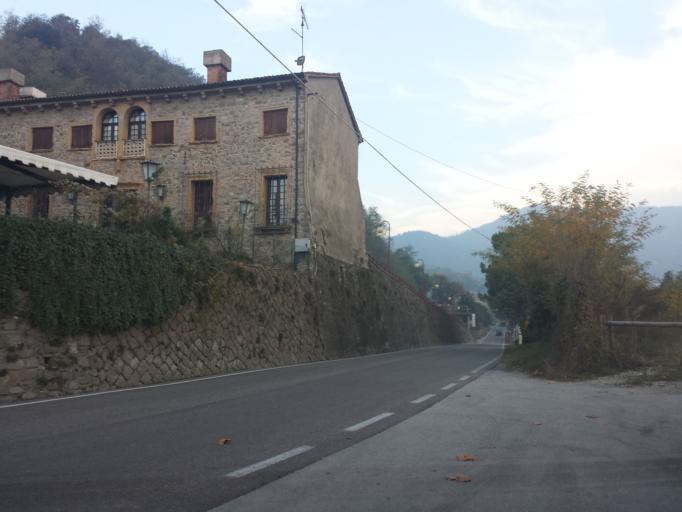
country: IT
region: Veneto
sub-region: Provincia di Padova
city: Vo
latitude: 45.3435
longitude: 11.6760
